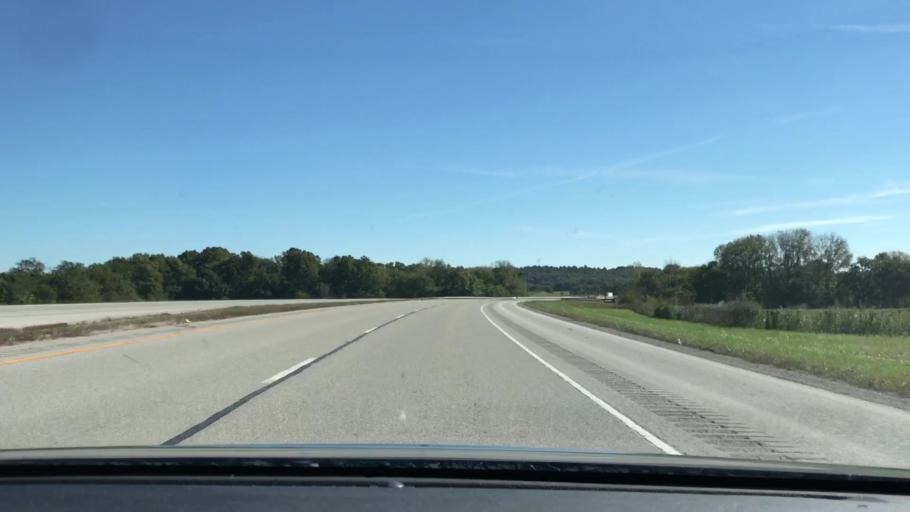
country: US
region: Kentucky
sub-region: Todd County
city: Elkton
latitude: 36.8244
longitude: -87.1592
